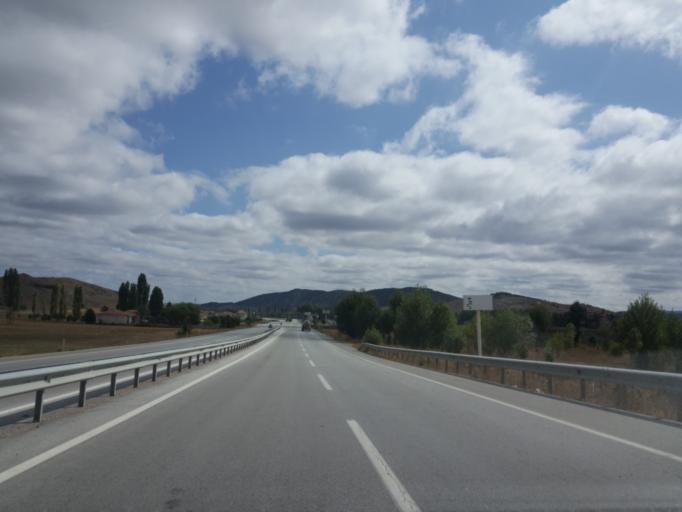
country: TR
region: Sivas
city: Yavu
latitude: 39.7958
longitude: 36.1905
